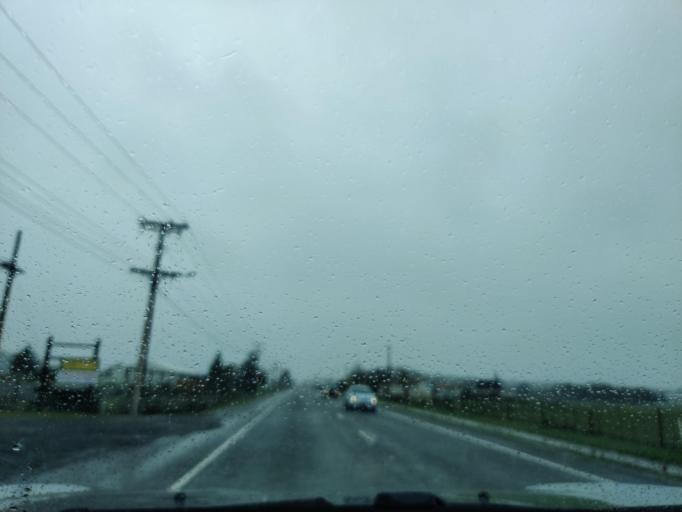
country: NZ
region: Hawke's Bay
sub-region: Hastings District
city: Hastings
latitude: -39.9922
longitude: 176.5384
